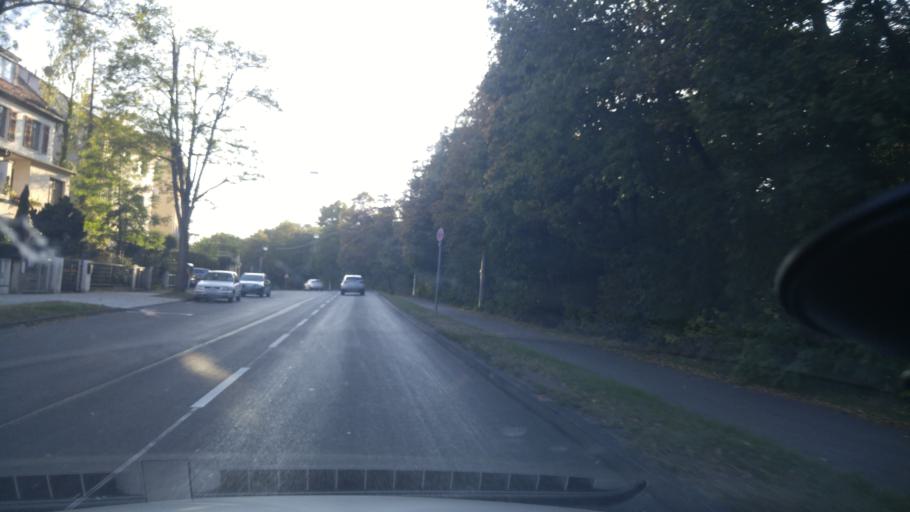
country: DE
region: Baden-Wuerttemberg
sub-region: Regierungsbezirk Stuttgart
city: Stuttgart Feuerbach
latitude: 48.7808
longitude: 9.1402
